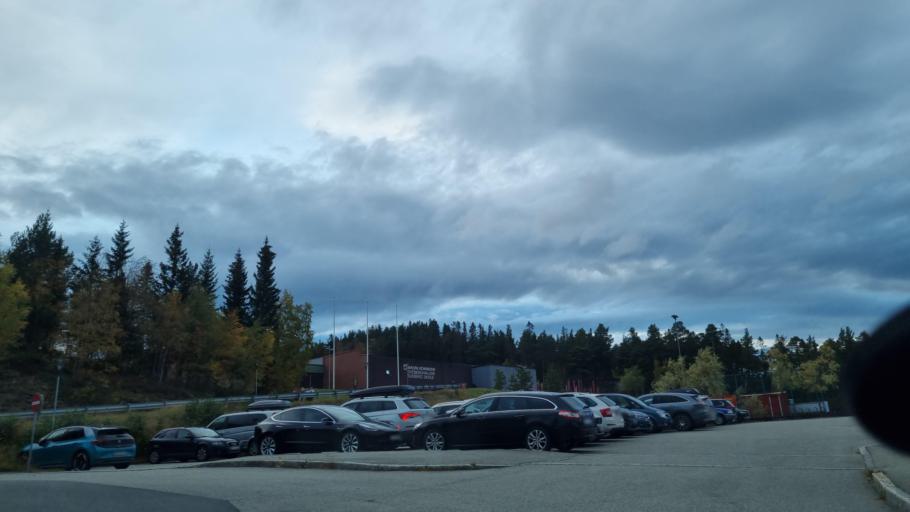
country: NO
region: Sor-Trondelag
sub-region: Malvik
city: Hommelvik
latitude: 63.4222
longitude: 10.7623
